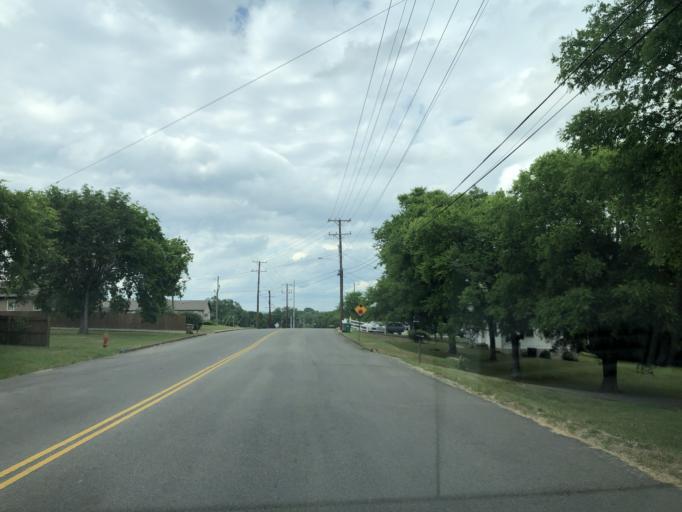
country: US
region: Tennessee
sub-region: Davidson County
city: Lakewood
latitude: 36.2613
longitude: -86.6909
